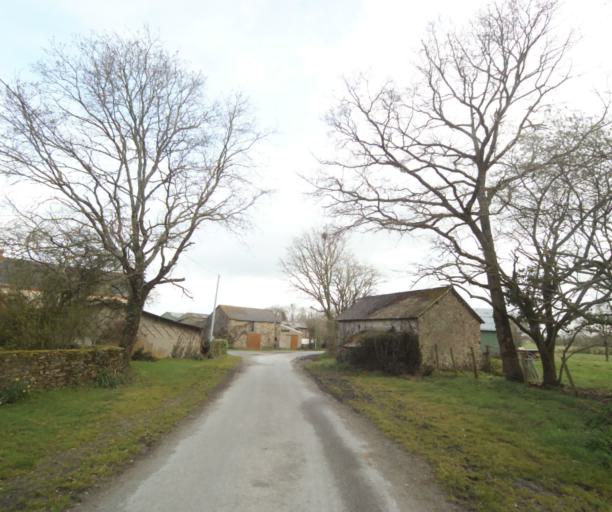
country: FR
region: Pays de la Loire
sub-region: Departement de la Loire-Atlantique
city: Bouvron
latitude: 47.4147
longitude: -1.8754
